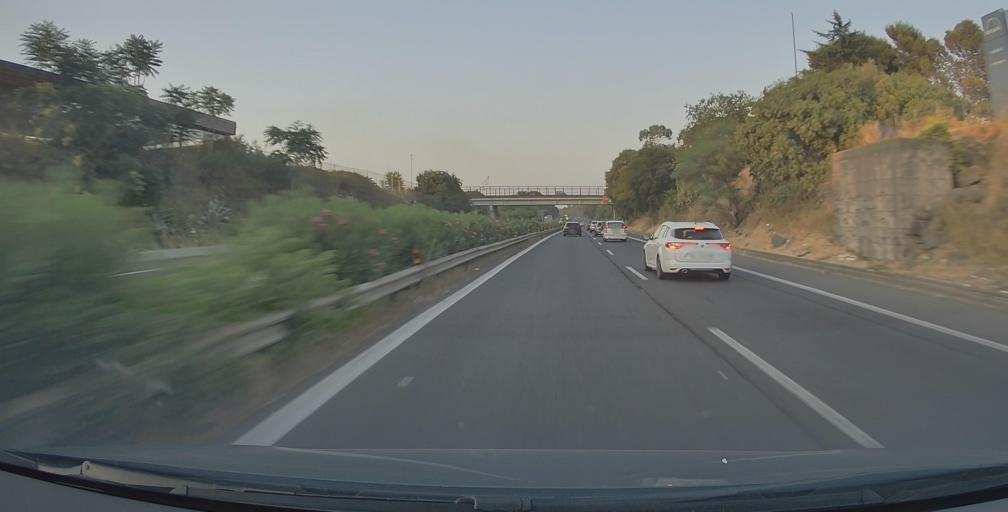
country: IT
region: Sicily
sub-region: Catania
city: San Gregorio di Catania
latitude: 37.5770
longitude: 15.1131
